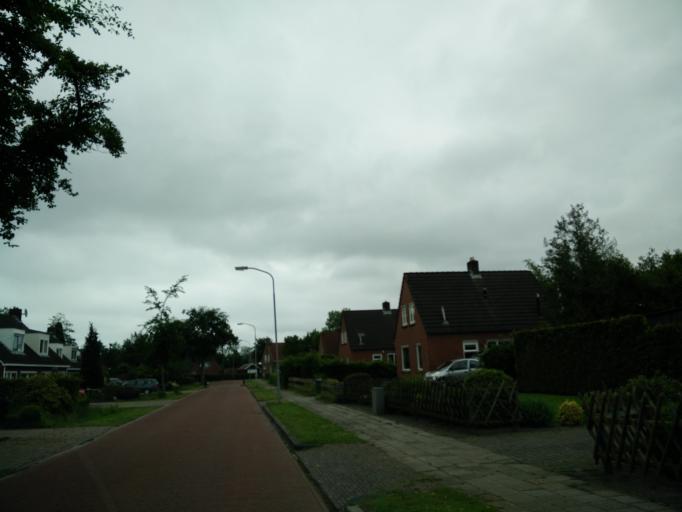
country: NL
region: Groningen
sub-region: Gemeente Leek
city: Leek
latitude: 53.1328
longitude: 6.4767
